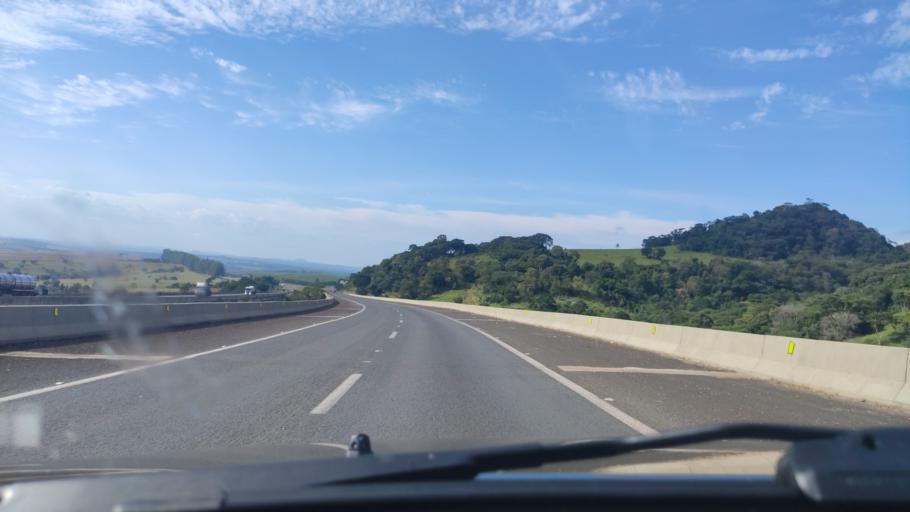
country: BR
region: Sao Paulo
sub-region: Itatinga
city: Itatinga
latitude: -23.1037
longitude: -48.5064
